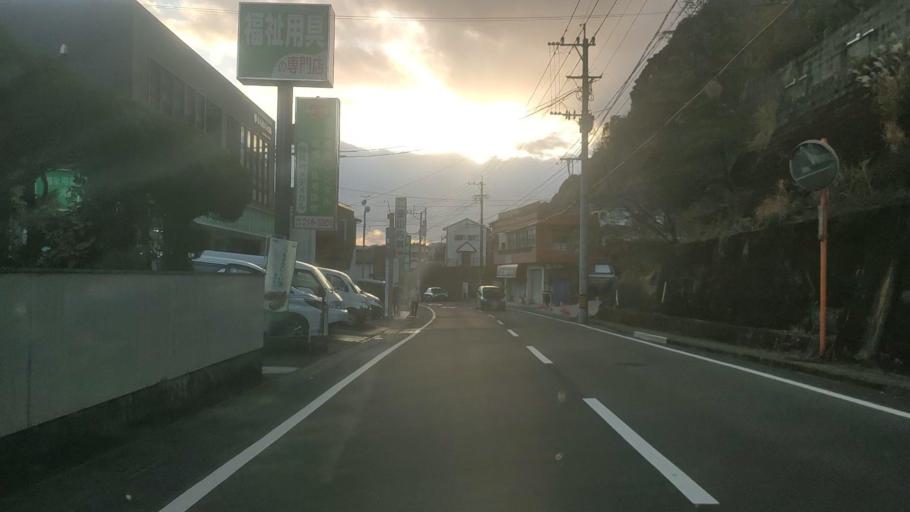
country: JP
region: Kagoshima
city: Kagoshima-shi
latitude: 31.6207
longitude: 130.5379
